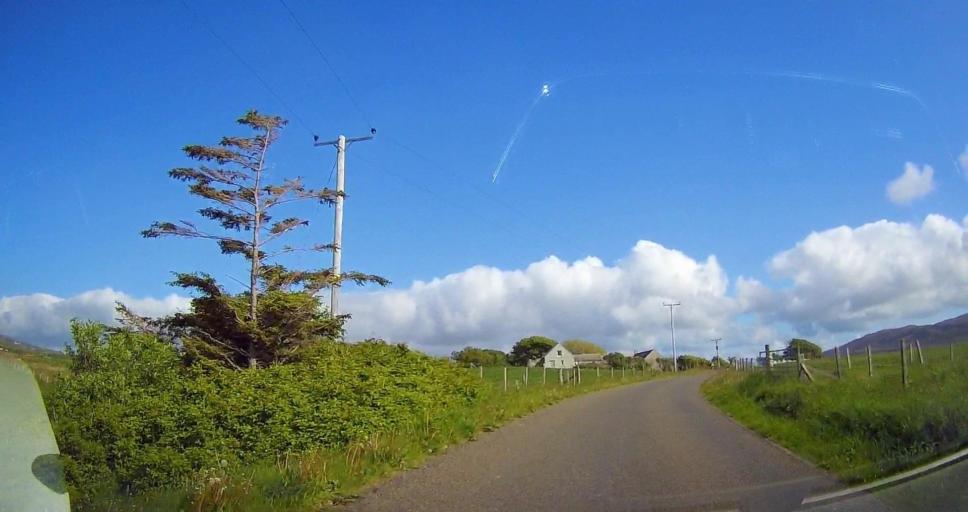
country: GB
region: Scotland
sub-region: Orkney Islands
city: Stromness
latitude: 58.9952
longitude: -3.1600
